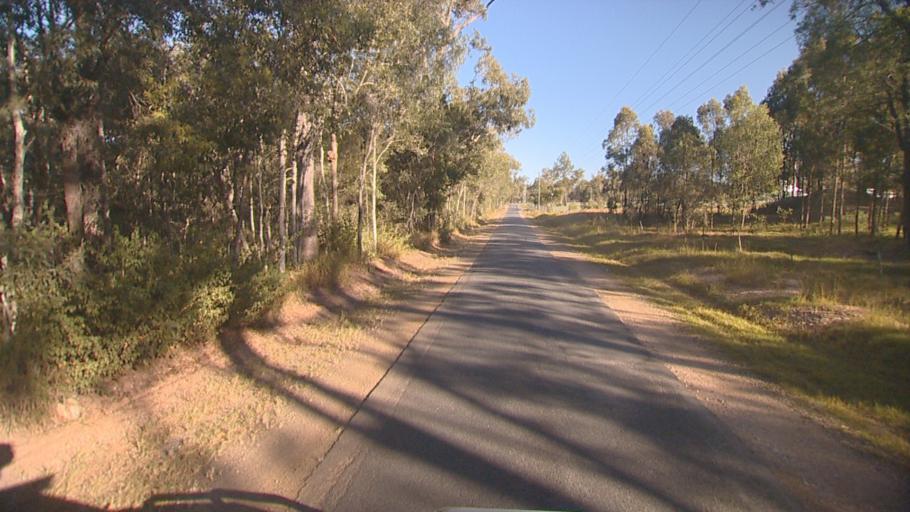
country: AU
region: Queensland
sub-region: Logan
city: North Maclean
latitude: -27.7883
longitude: 153.0385
